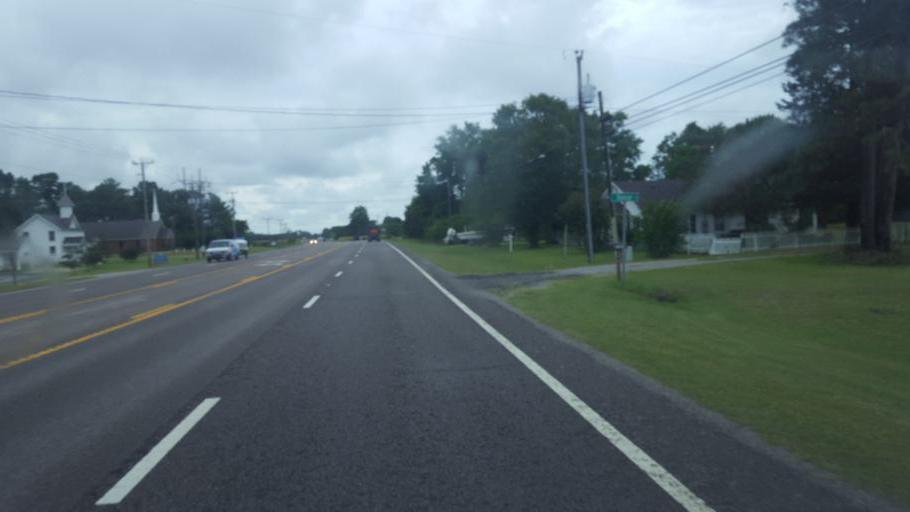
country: US
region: North Carolina
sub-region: Dare County
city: Southern Shores
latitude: 36.1855
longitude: -75.8640
